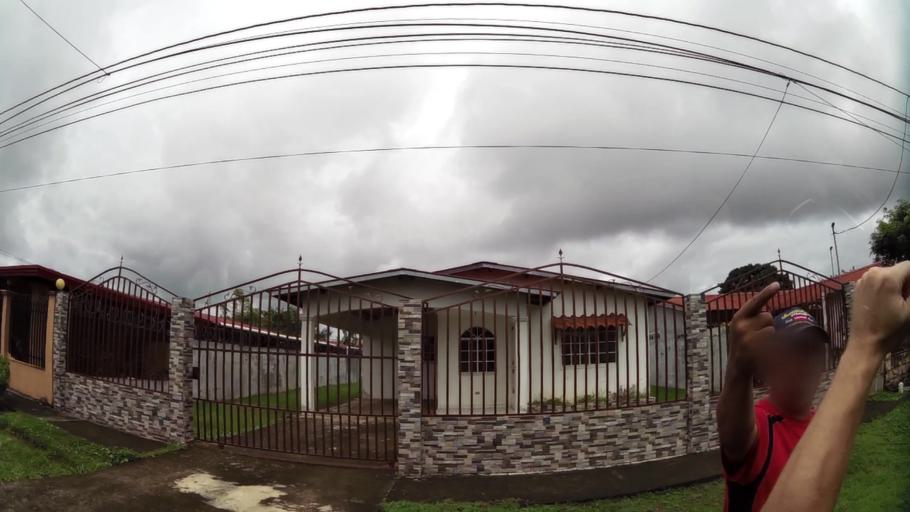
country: PA
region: Chiriqui
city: David
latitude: 8.4164
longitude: -82.4522
